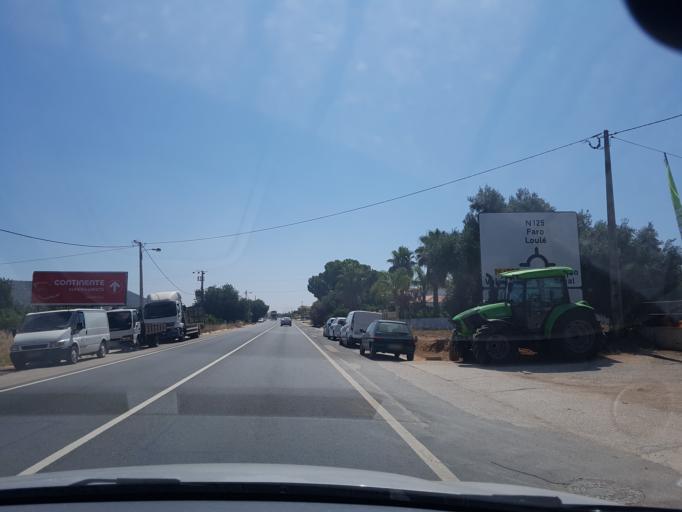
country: PT
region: Faro
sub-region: Loule
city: Vilamoura
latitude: 37.1097
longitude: -8.0935
